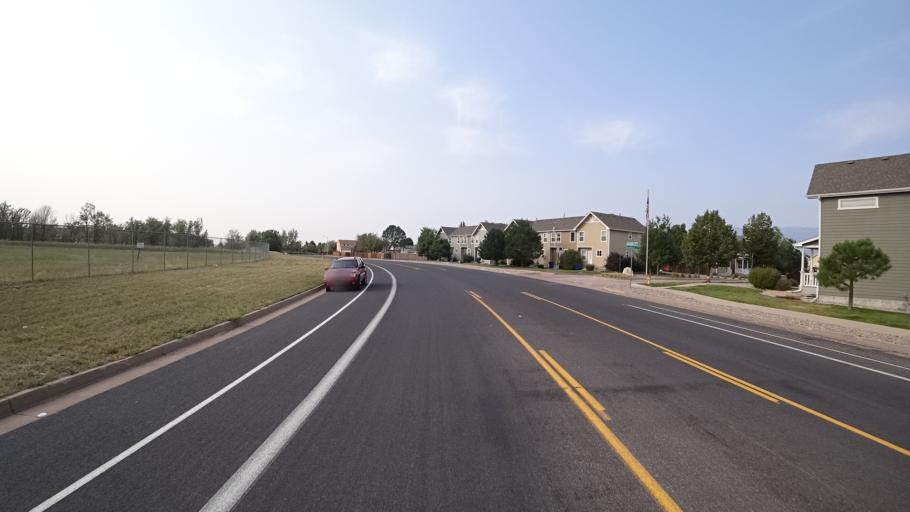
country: US
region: Colorado
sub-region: El Paso County
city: Cimarron Hills
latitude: 38.8116
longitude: -104.7334
